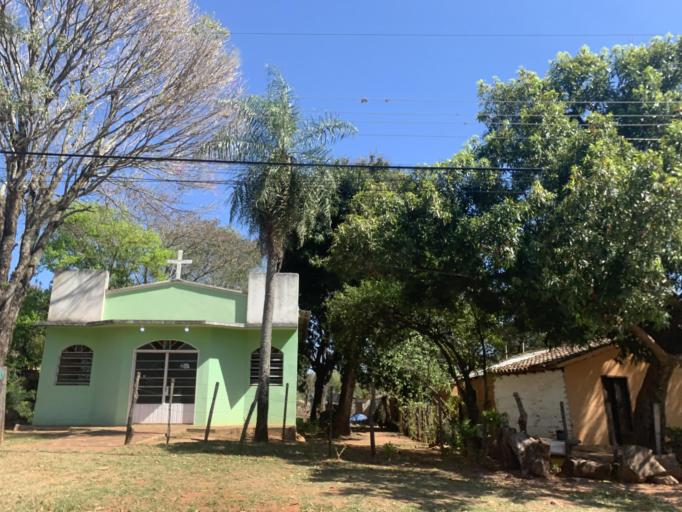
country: PY
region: Misiones
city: San Juan Bautista
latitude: -26.6632
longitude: -57.1439
